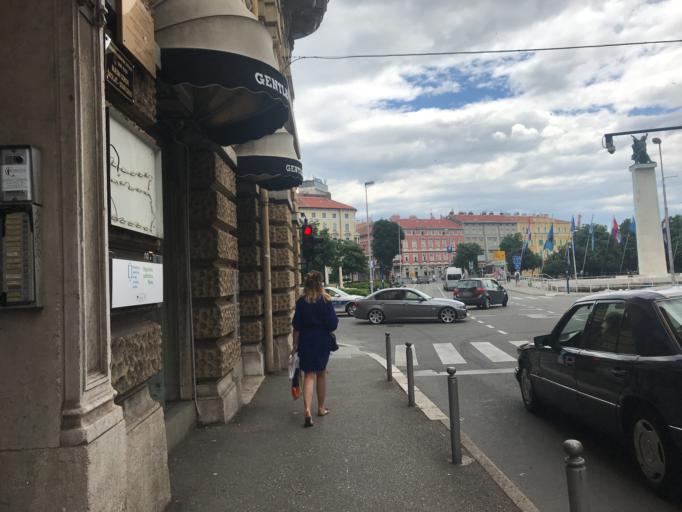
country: HR
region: Primorsko-Goranska
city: Drenova
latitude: 45.3271
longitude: 14.4471
